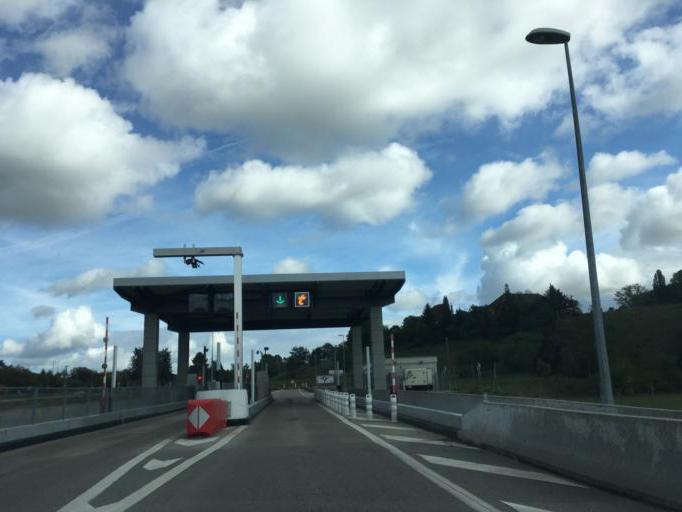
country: FR
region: Rhone-Alpes
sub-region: Departement de l'Isere
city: La Tour-du-Pin
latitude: 45.5568
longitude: 5.4640
